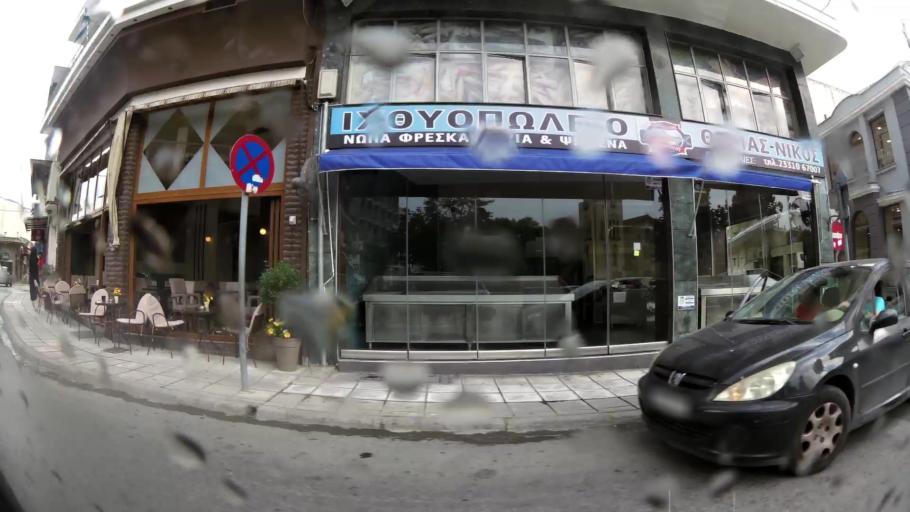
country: GR
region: Central Macedonia
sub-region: Nomos Imathias
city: Veroia
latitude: 40.5254
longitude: 22.2028
